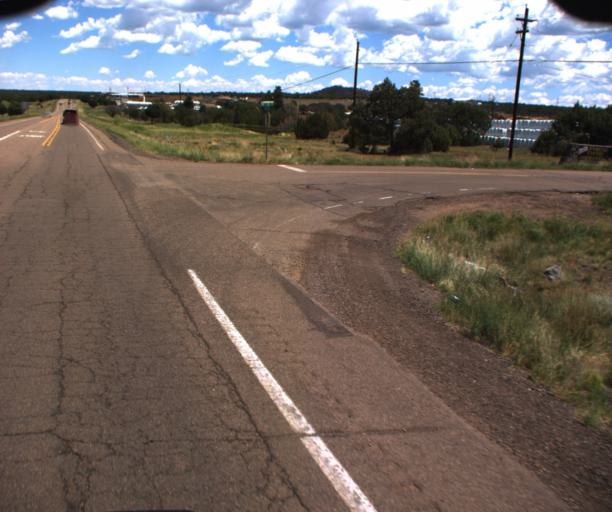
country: US
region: Arizona
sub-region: Navajo County
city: Show Low
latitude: 34.2603
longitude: -109.9992
